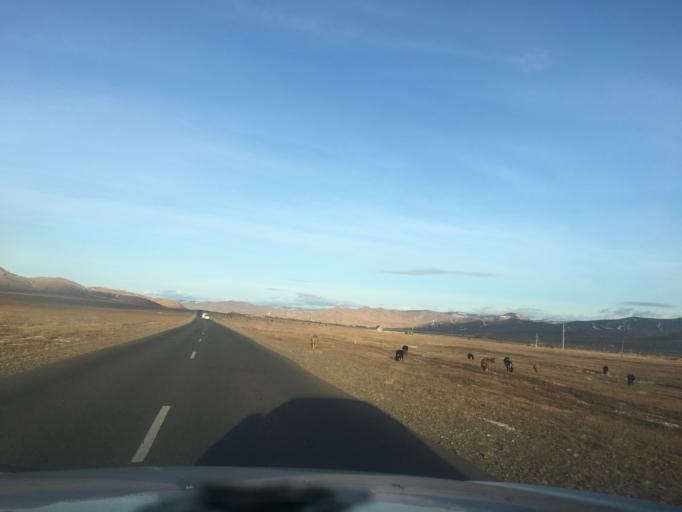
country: MN
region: Central Aimak
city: Mandal
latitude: 48.0939
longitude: 106.6086
